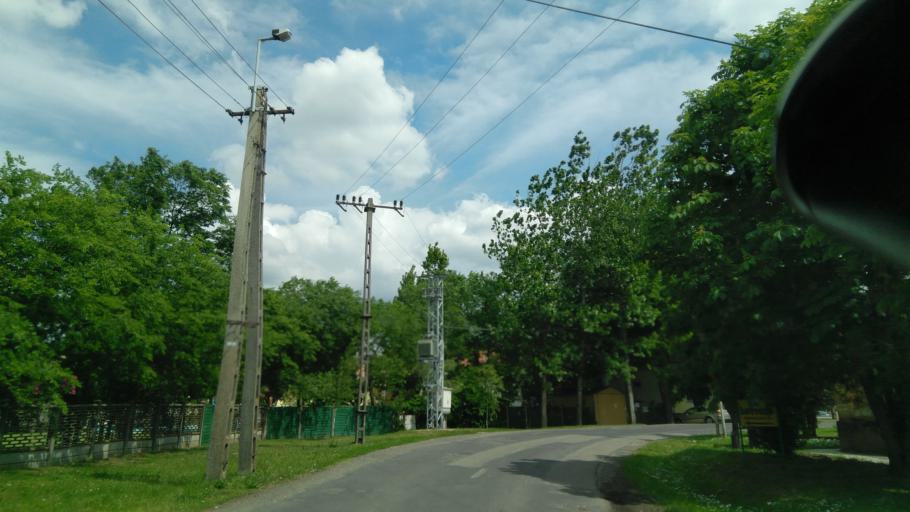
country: HU
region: Bekes
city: Totkomlos
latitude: 46.4113
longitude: 20.7339
